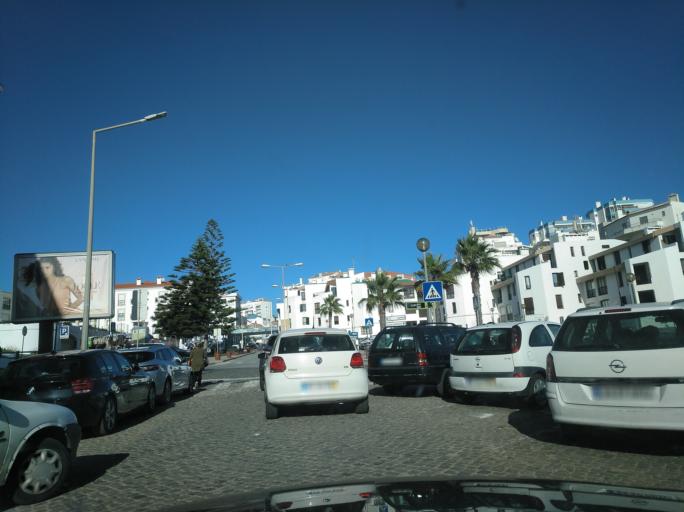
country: PT
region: Lisbon
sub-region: Mafra
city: Ericeira
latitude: 38.9607
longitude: -9.4173
